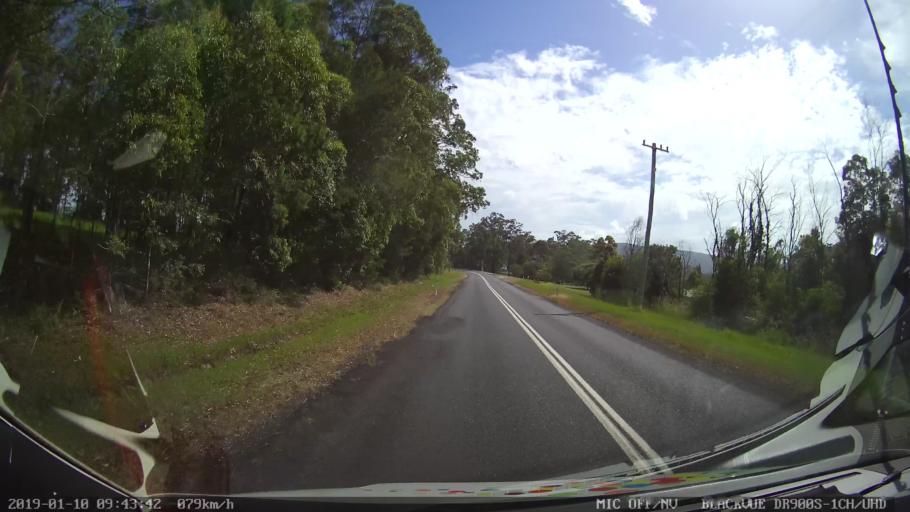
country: AU
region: New South Wales
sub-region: Coffs Harbour
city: Nana Glen
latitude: -30.1258
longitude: 153.0007
